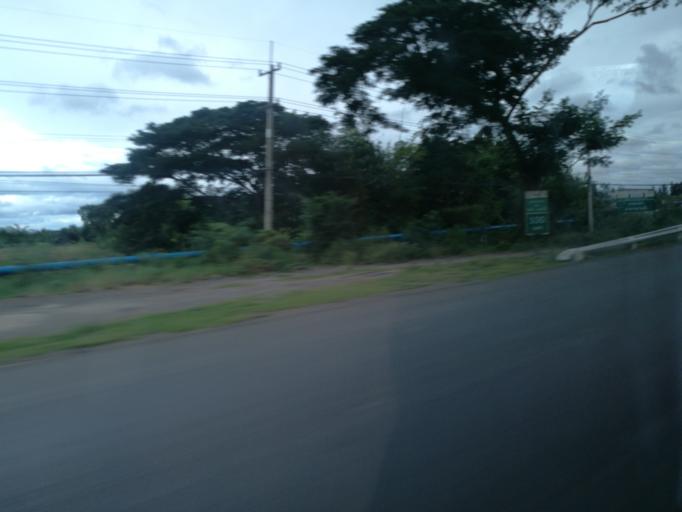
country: TH
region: Prachuap Khiri Khan
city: Sam Roi Yot
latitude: 12.3156
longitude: 99.8780
